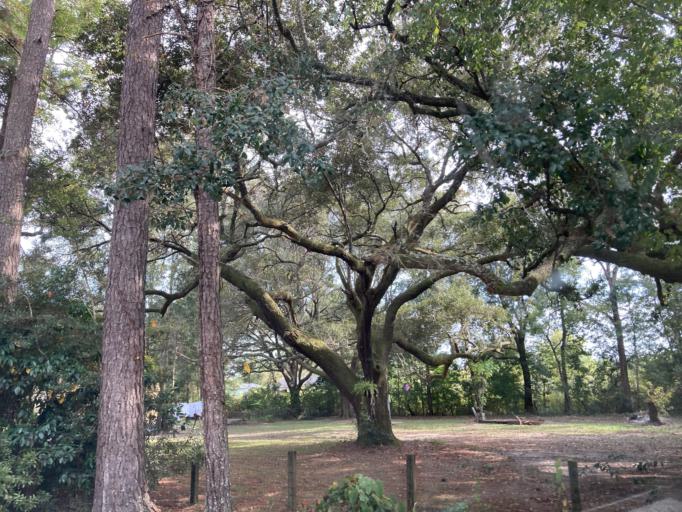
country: US
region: Mississippi
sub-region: Jackson County
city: Saint Martin
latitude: 30.4811
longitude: -88.8593
